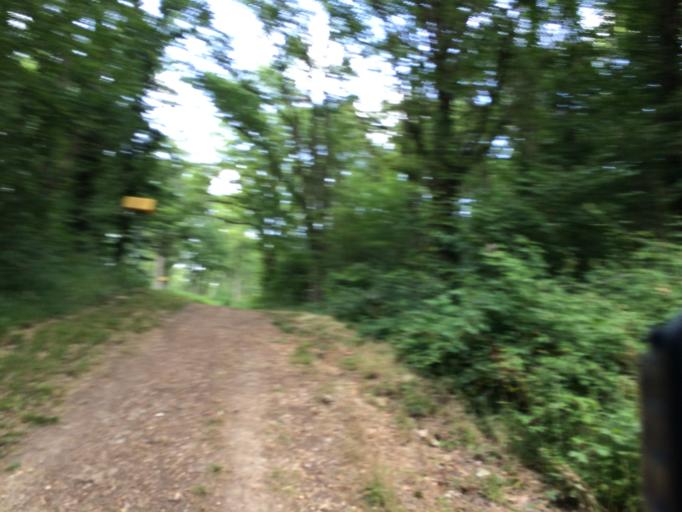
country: FR
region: Ile-de-France
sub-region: Departement de l'Essonne
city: Etiolles
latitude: 48.6413
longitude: 2.4906
